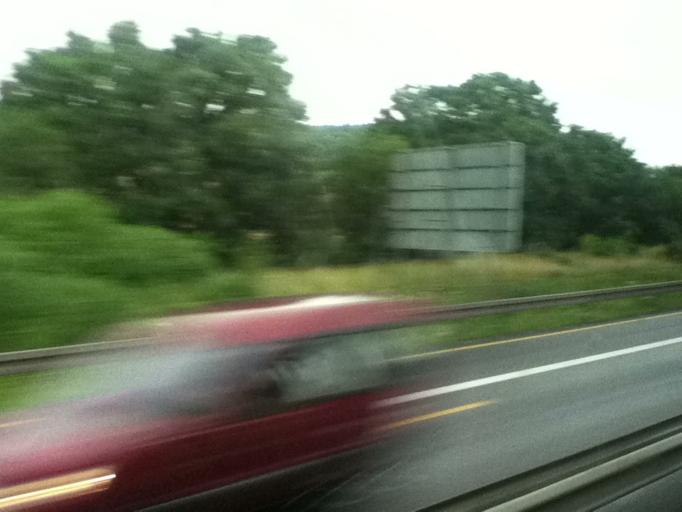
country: DE
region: Thuringia
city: Wandersleben
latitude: 50.8779
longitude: 10.8174
